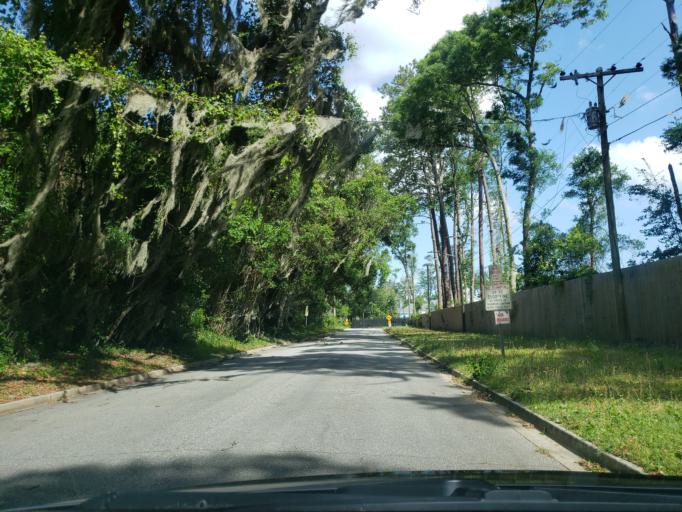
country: US
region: Georgia
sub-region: Chatham County
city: Thunderbolt
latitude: 32.0184
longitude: -81.0634
